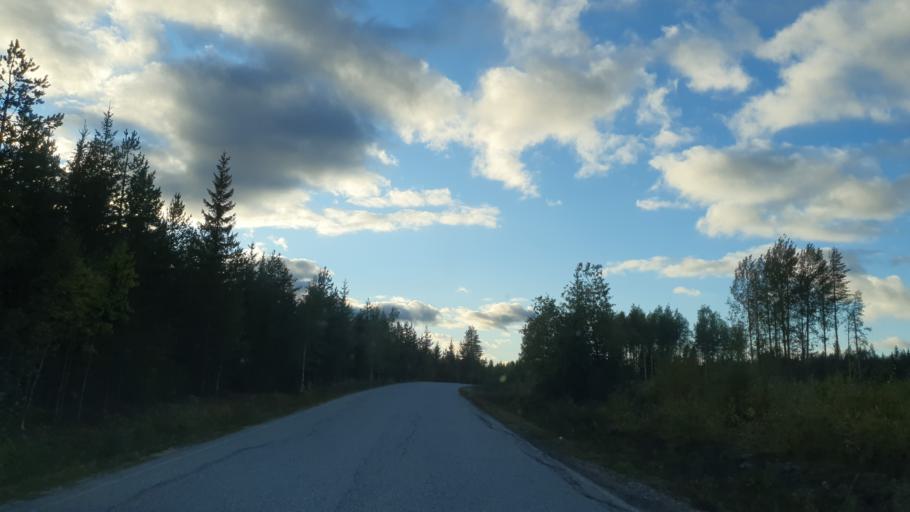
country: FI
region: Kainuu
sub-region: Kehys-Kainuu
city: Kuhmo
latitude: 63.9500
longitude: 29.7533
